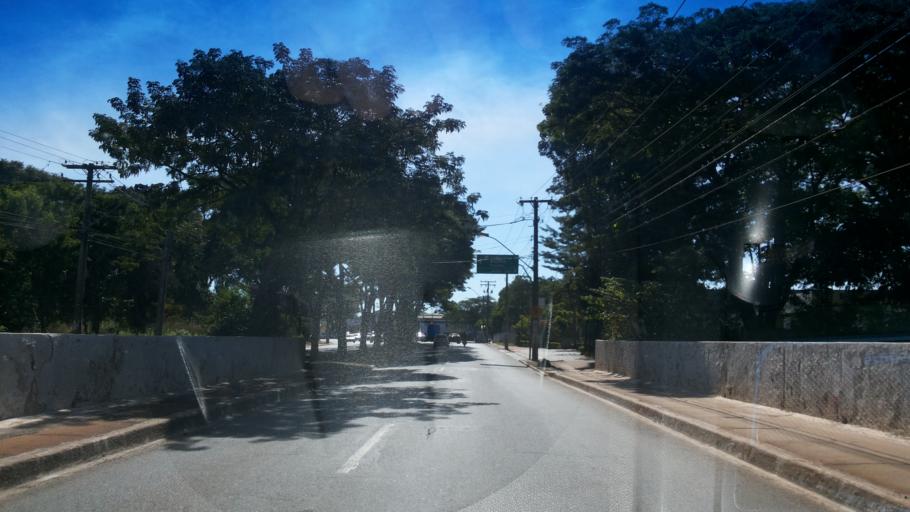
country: BR
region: Goias
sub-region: Goiania
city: Goiania
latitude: -16.6482
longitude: -49.2424
